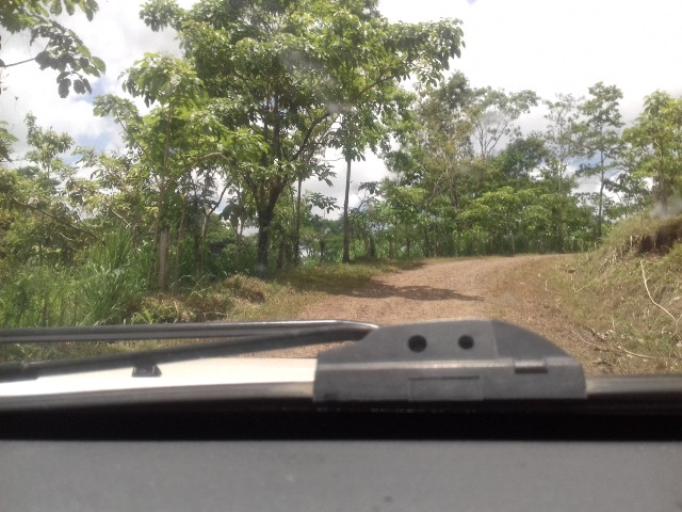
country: NI
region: Matagalpa
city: Matiguas
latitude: 13.0097
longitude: -85.3955
